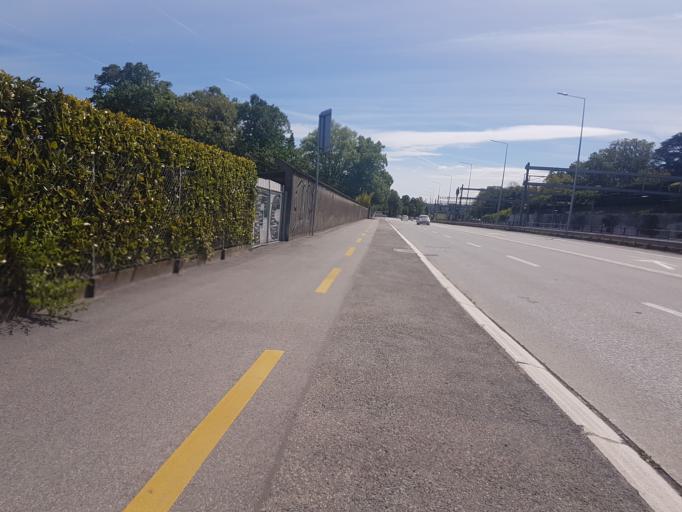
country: CH
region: Geneva
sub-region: Geneva
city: Bellevue
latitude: 46.2653
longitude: 6.1624
